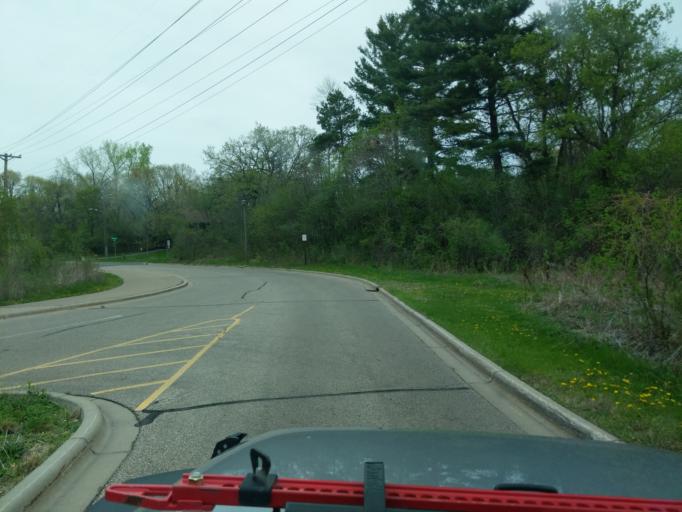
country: US
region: Minnesota
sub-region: Anoka County
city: Coon Rapids
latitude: 45.1478
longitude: -93.3081
